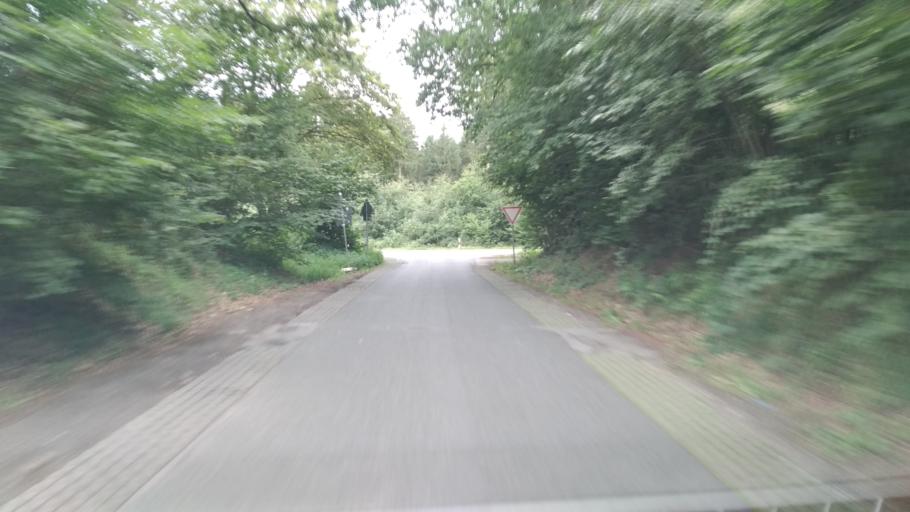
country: DE
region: Schleswig-Holstein
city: Neuberend
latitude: 54.5273
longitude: 9.5230
